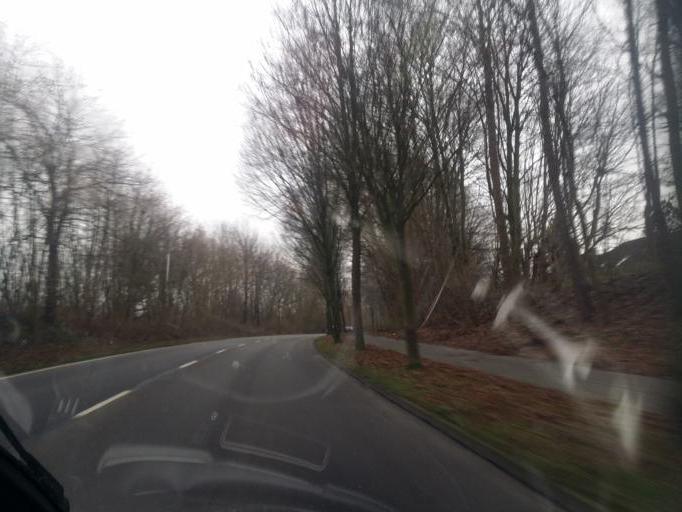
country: DE
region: Schleswig-Holstein
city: Heide
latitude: 54.2017
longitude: 9.1232
